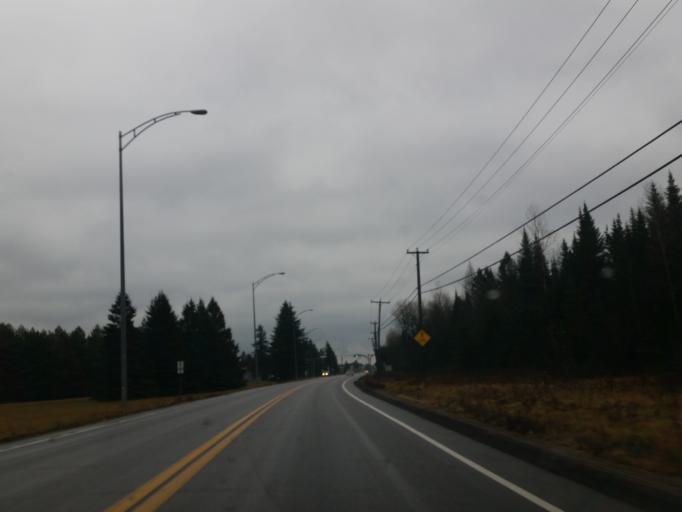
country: CA
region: Quebec
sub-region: Capitale-Nationale
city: Shannon
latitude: 46.8851
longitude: -71.4921
